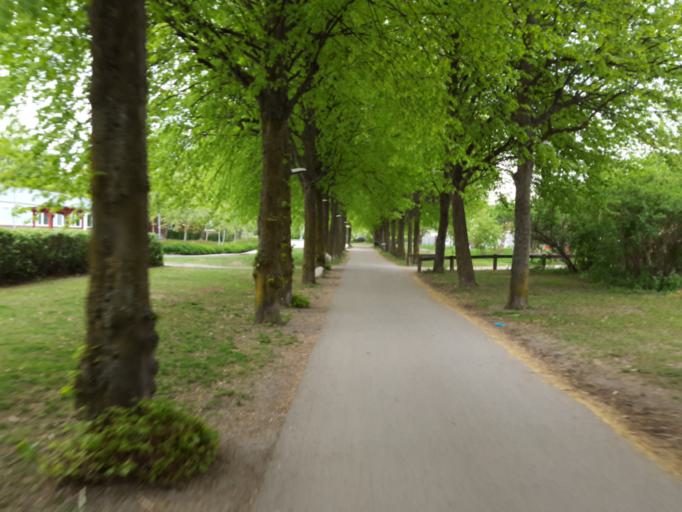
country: SE
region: Uppsala
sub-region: Uppsala Kommun
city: Uppsala
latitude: 59.8687
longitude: 17.6537
